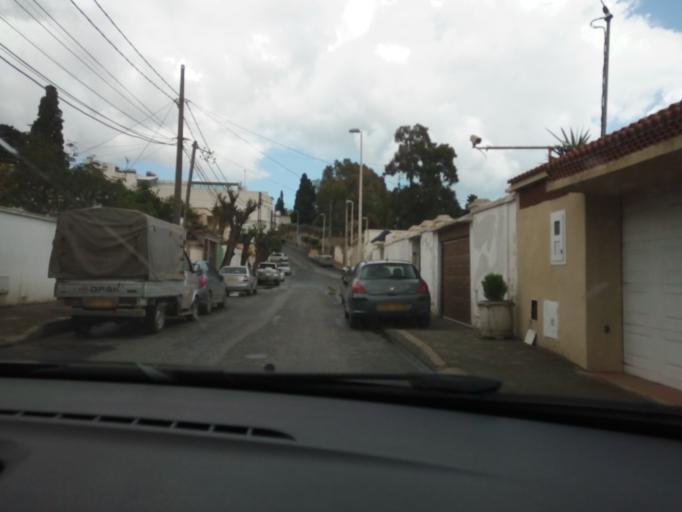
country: DZ
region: Alger
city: Algiers
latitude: 36.7516
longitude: 3.0248
